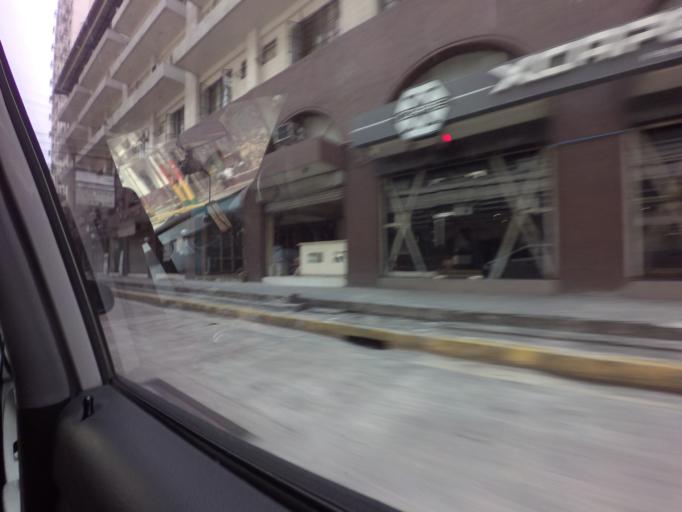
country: PH
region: Metro Manila
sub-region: City of Manila
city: Port Area
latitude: 14.5749
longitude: 120.9901
